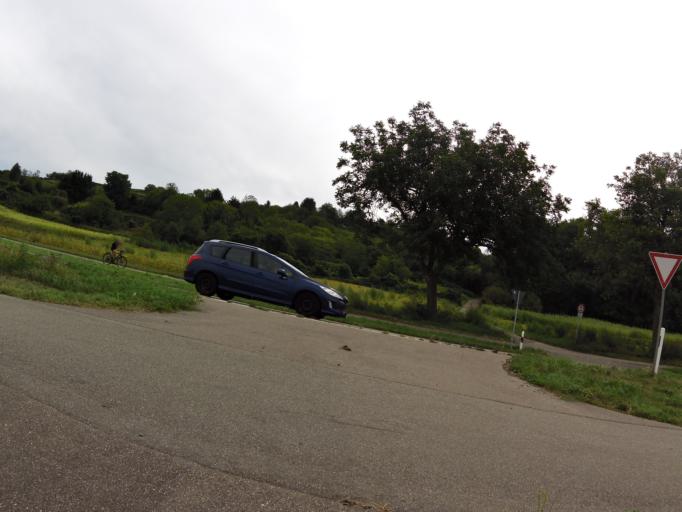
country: DE
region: Baden-Wuerttemberg
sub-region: Freiburg Region
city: Lahr
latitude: 48.3526
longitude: 7.8469
